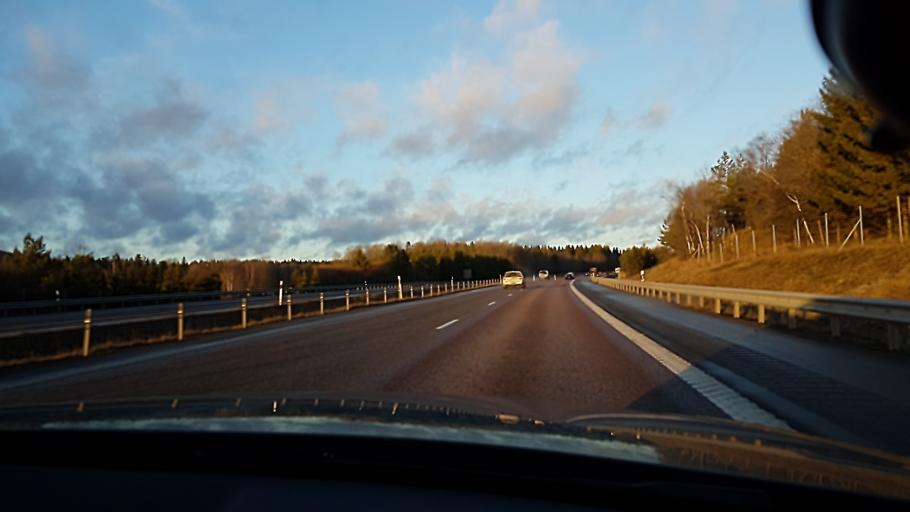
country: SE
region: Soedermanland
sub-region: Trosa Kommun
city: Vagnharad
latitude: 59.0463
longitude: 17.5658
